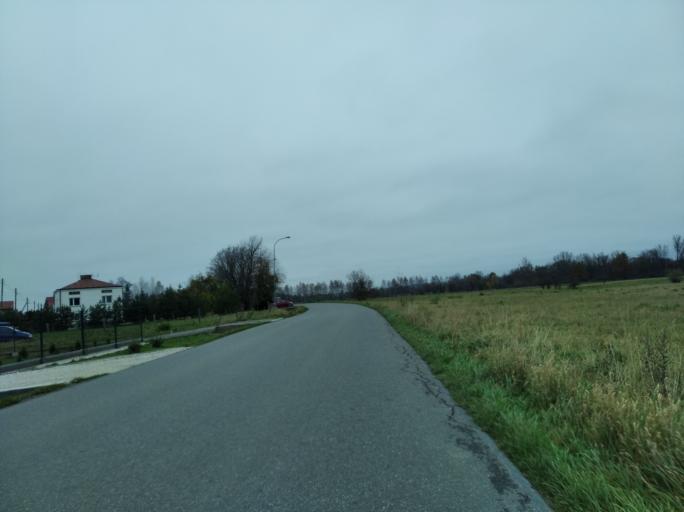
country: PL
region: Subcarpathian Voivodeship
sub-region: Powiat krosnienski
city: Chorkowka
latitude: 49.6813
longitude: 21.6766
